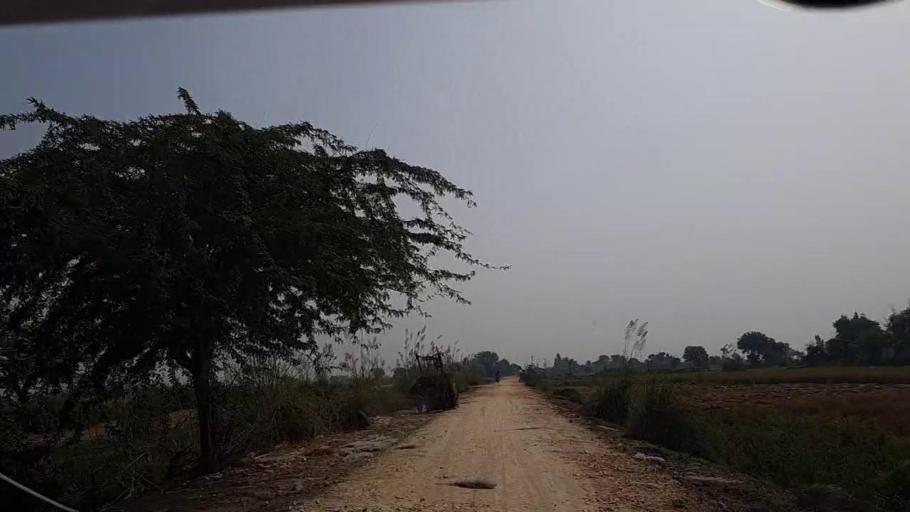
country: PK
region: Sindh
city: Garhi Yasin
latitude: 27.9250
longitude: 68.5668
